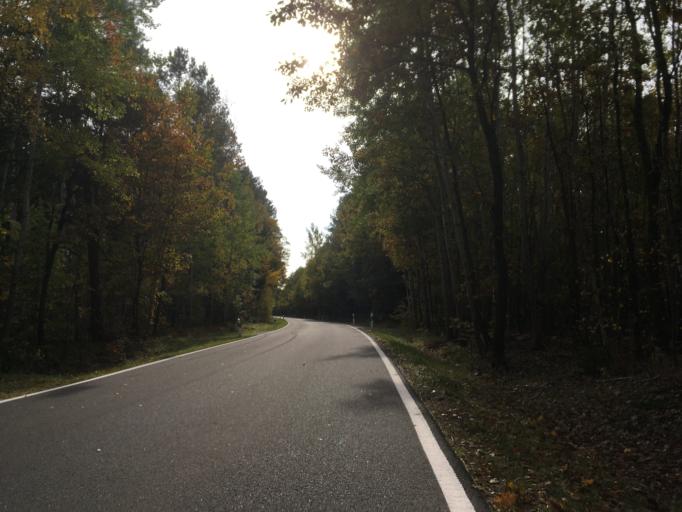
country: DE
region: Brandenburg
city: Templin
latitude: 53.0139
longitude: 13.4658
